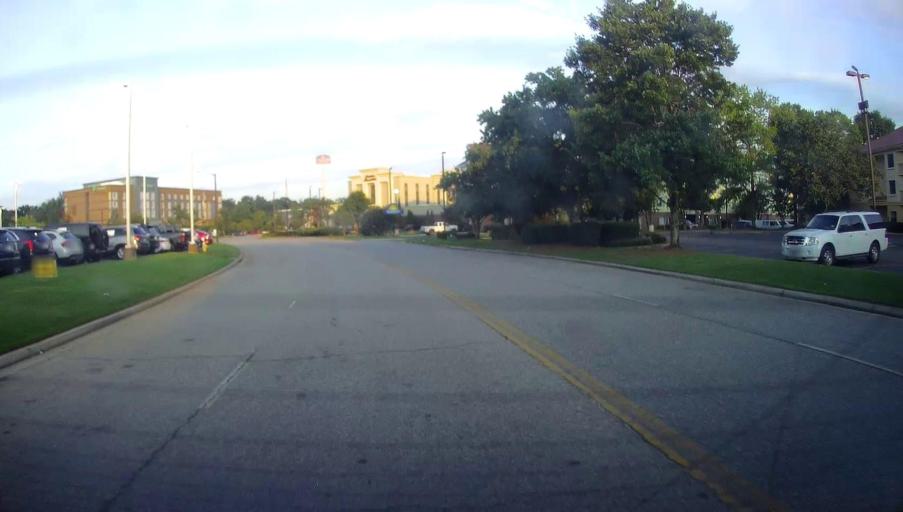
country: US
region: Georgia
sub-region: Bibb County
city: Macon
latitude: 32.9045
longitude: -83.6845
